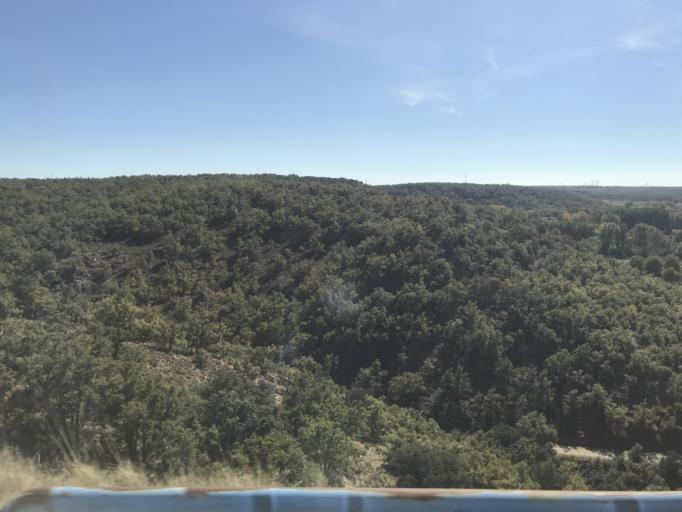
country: ES
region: Castille and Leon
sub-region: Provincia de Soria
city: Arcos de Jalon
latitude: 41.1325
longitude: -2.3324
